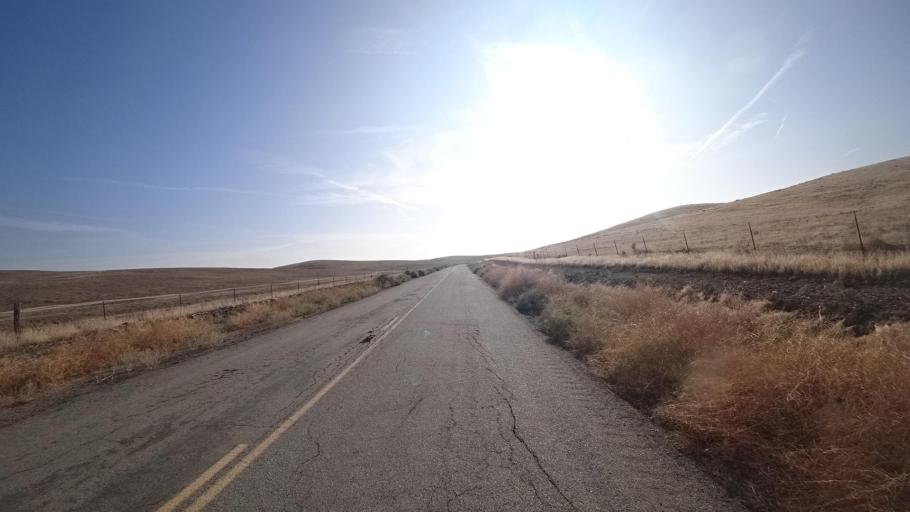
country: US
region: California
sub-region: Tulare County
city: Richgrove
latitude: 35.6371
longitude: -119.0388
